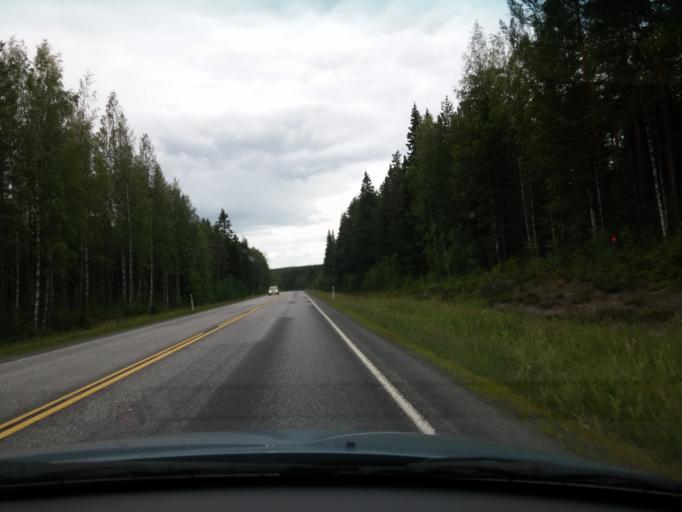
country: FI
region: Central Finland
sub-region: AEaenekoski
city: AEaenekoski
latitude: 62.7283
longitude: 25.7617
